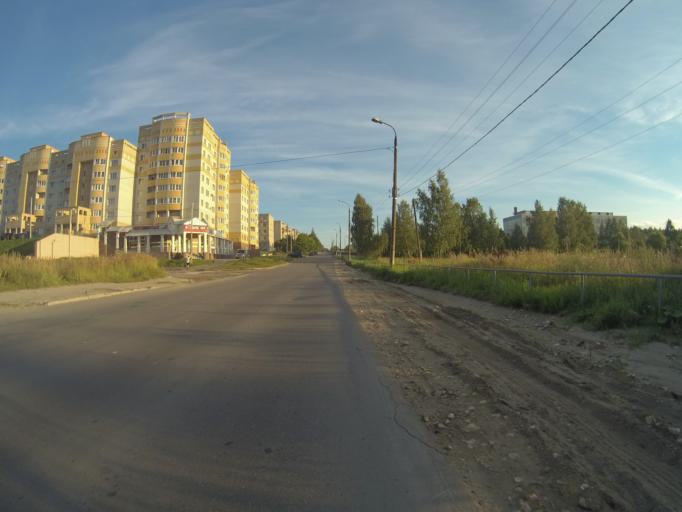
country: RU
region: Vladimir
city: Kommunar
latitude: 56.0640
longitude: 40.4877
